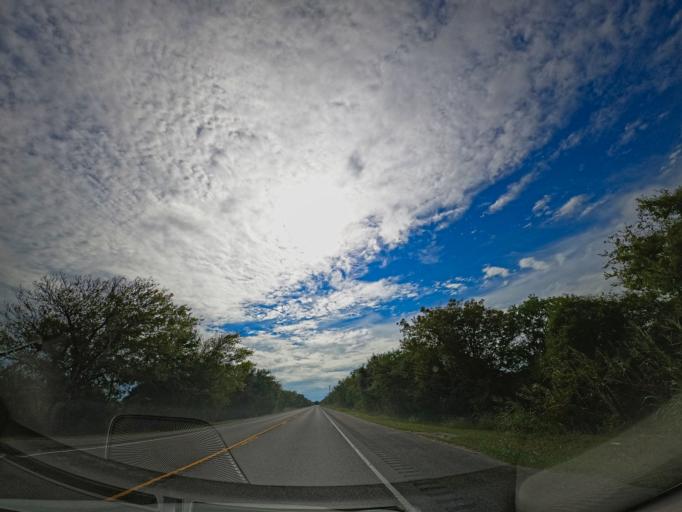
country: US
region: Louisiana
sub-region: Saint Tammany Parish
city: Eden Isle
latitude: 30.0742
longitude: -89.7963
